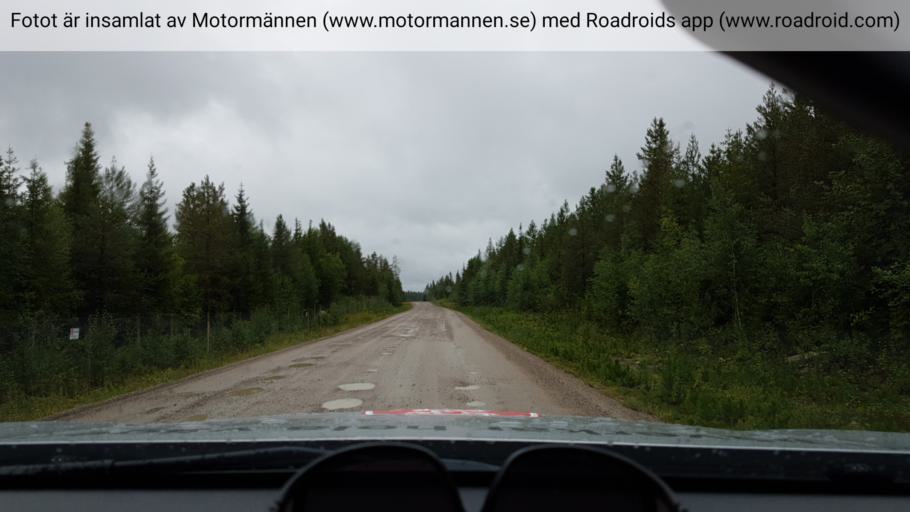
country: SE
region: Vaesterbotten
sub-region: Lycksele Kommun
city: Soderfors
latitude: 64.7673
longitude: 17.6596
